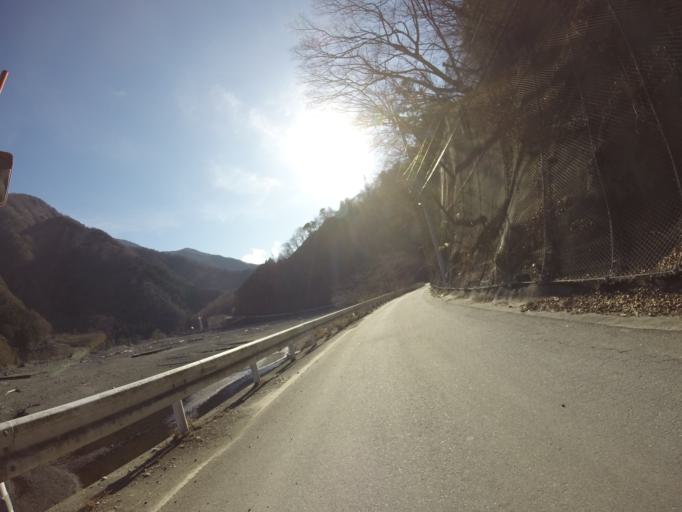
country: JP
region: Yamanashi
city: Ryuo
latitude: 35.4029
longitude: 138.3266
